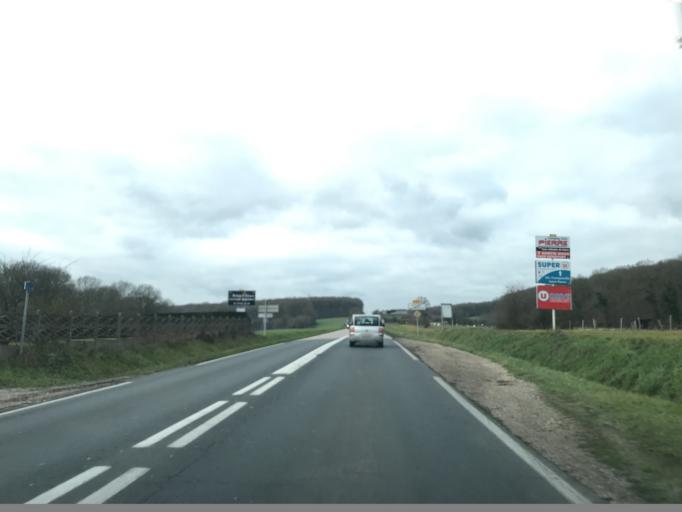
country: FR
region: Haute-Normandie
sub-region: Departement de l'Eure
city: Fleury-sur-Andelle
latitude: 49.3658
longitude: 1.3486
